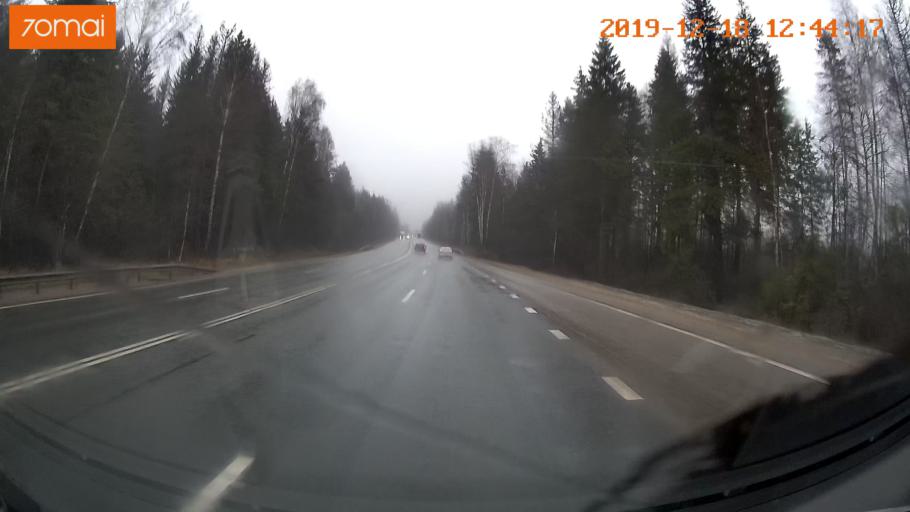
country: RU
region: Moskovskaya
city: Vysokovsk
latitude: 56.2175
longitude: 36.6477
